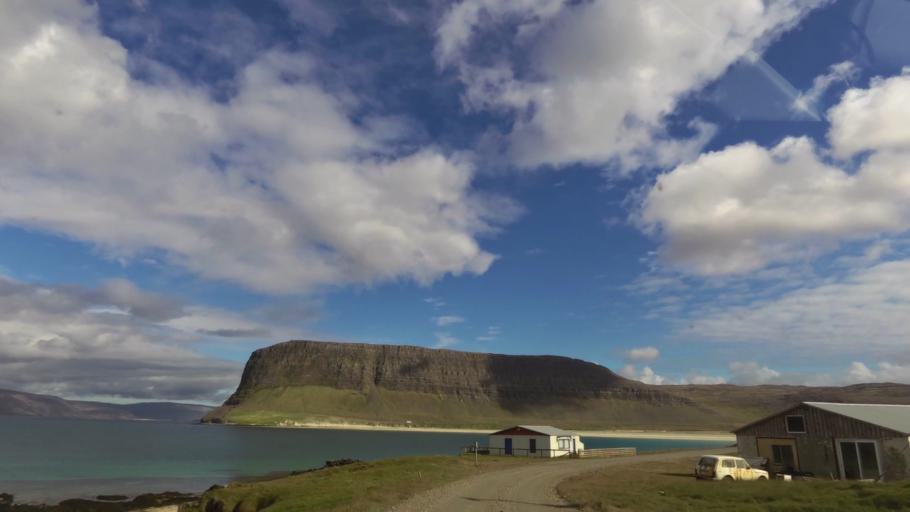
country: IS
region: West
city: Olafsvik
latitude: 65.5914
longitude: -24.1242
